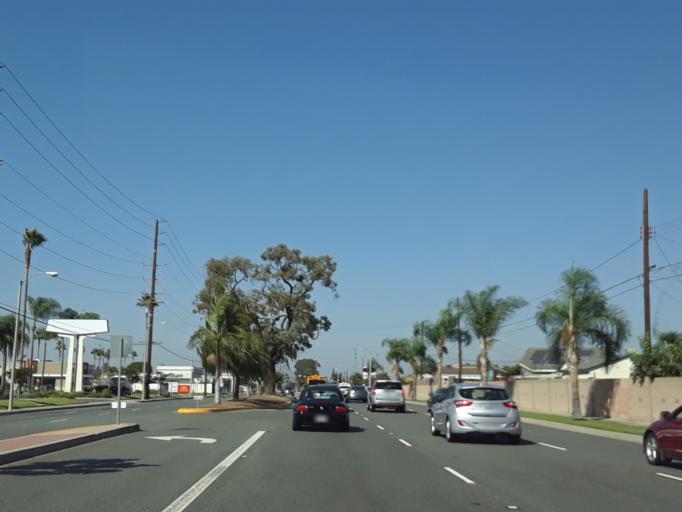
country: US
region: California
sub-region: Orange County
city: Cypress
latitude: 33.8136
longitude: -118.0282
